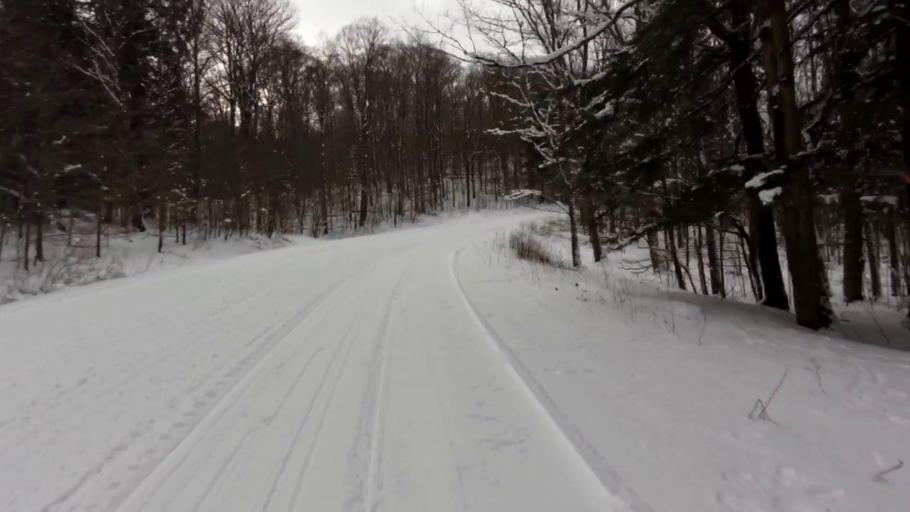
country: US
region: New York
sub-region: Cattaraugus County
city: Salamanca
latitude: 42.0681
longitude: -78.7608
